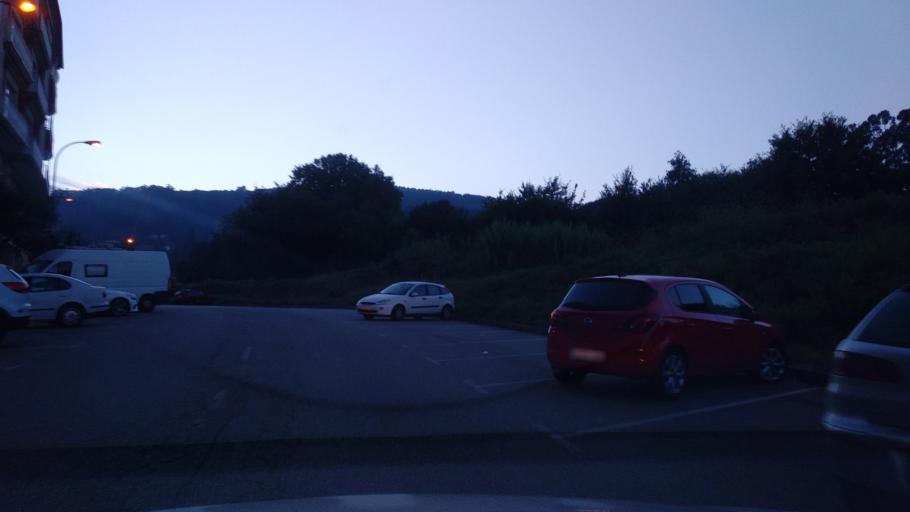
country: ES
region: Galicia
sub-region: Provincia de Pontevedra
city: Moana
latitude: 42.2897
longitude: -8.7329
